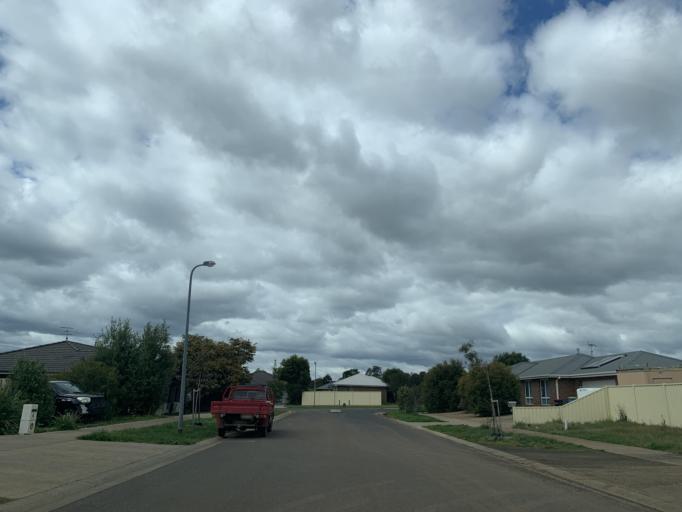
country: AU
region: Victoria
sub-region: Whittlesea
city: Whittlesea
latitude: -37.2910
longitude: 144.9349
